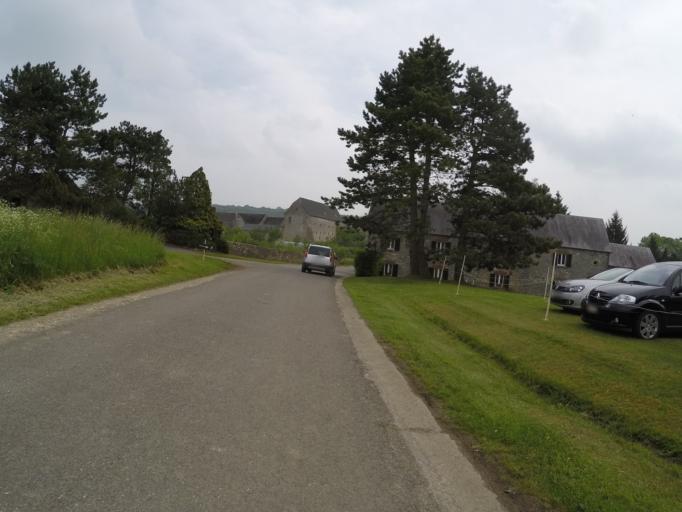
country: BE
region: Wallonia
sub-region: Province de Namur
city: Ciney
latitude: 50.3267
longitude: 5.0671
